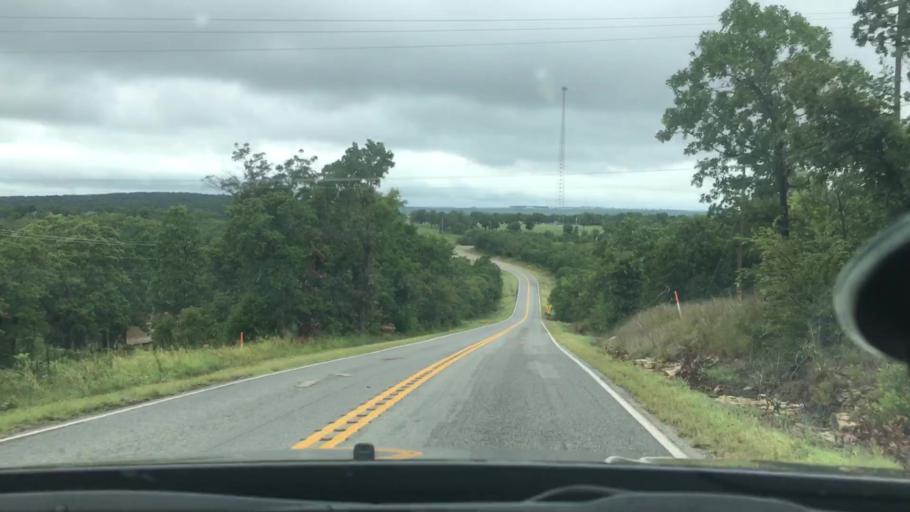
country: US
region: Oklahoma
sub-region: Sequoyah County
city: Vian
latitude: 35.6239
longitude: -94.9615
